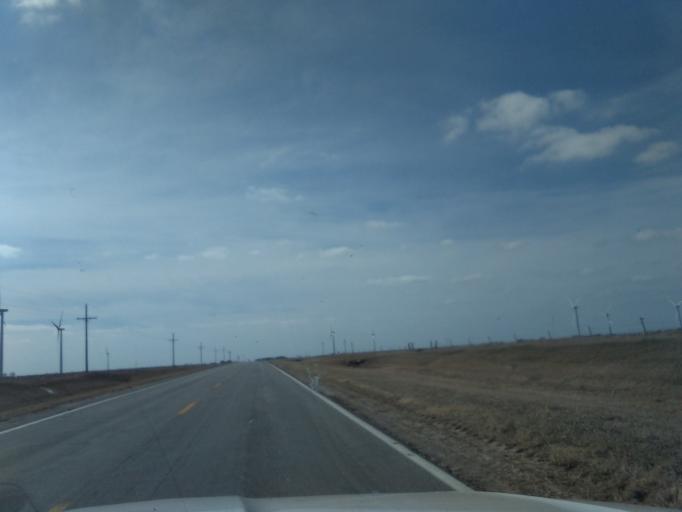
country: US
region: Nebraska
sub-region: Gage County
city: Wymore
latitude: 40.0455
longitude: -96.9042
